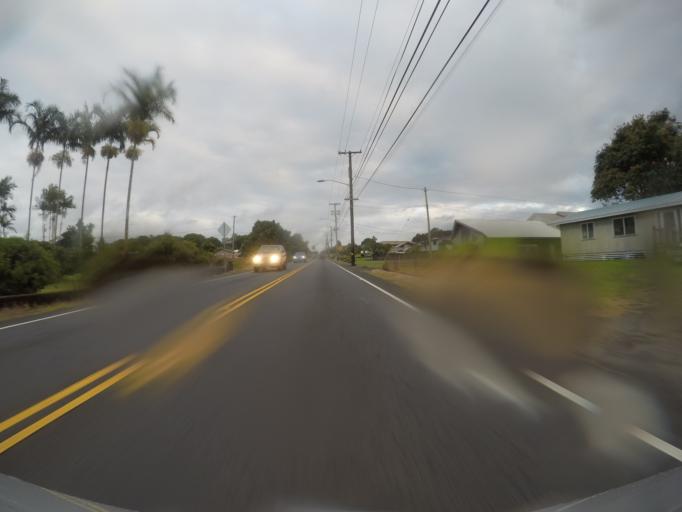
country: US
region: Hawaii
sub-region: Hawaii County
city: Hilo
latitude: 19.6923
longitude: -155.0904
